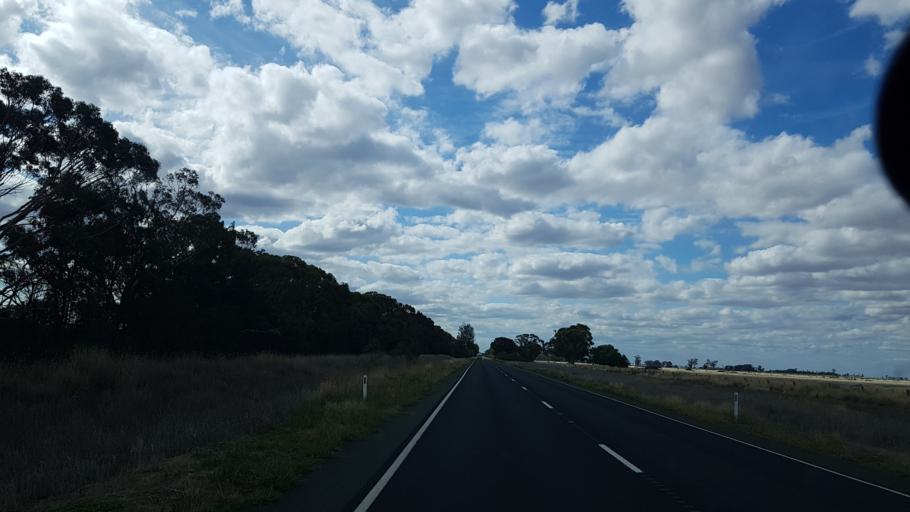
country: AU
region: Victoria
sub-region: Swan Hill
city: Swan Hill
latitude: -35.9844
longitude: 143.9454
